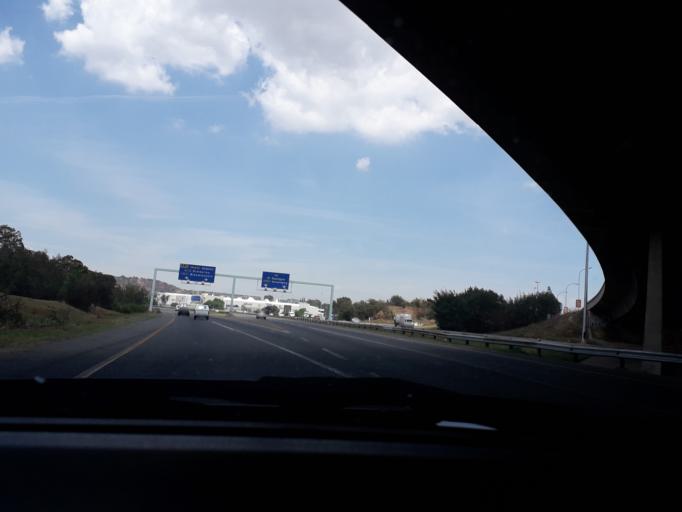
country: ZA
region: Gauteng
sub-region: City of Johannesburg Metropolitan Municipality
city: Johannesburg
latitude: -26.2586
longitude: 27.9879
